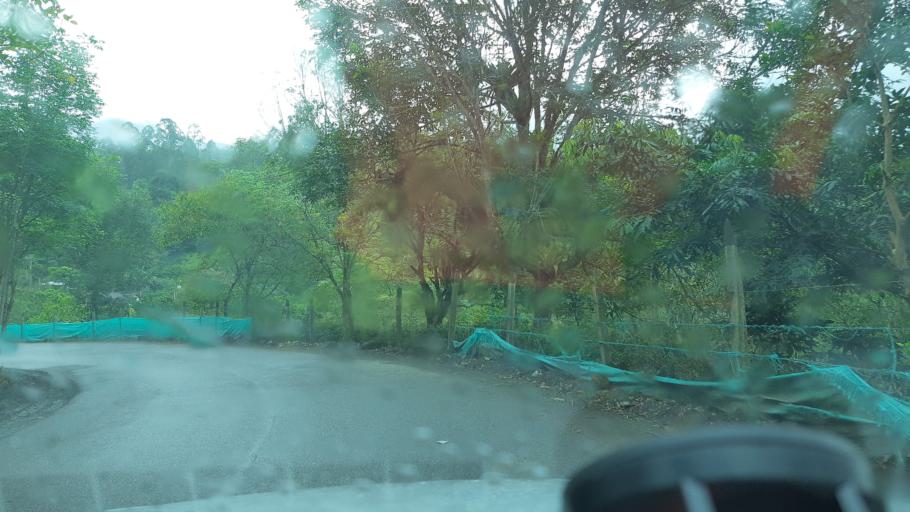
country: CO
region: Boyaca
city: Chinavita
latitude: 5.1515
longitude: -73.3633
